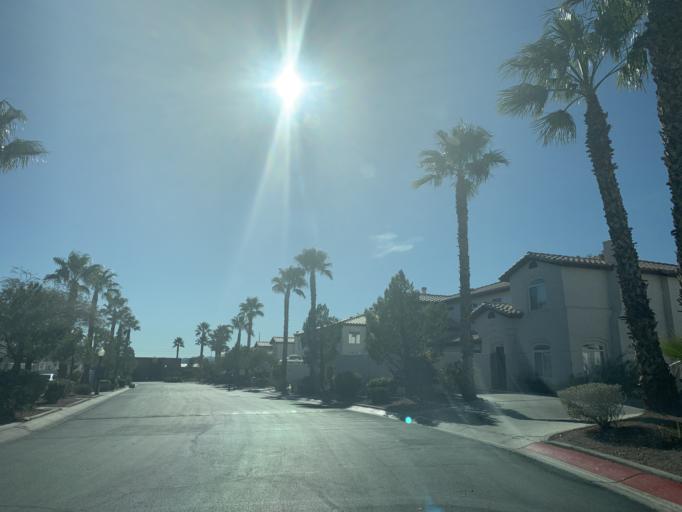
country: US
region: Nevada
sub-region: Clark County
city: Summerlin South
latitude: 36.1184
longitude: -115.2977
